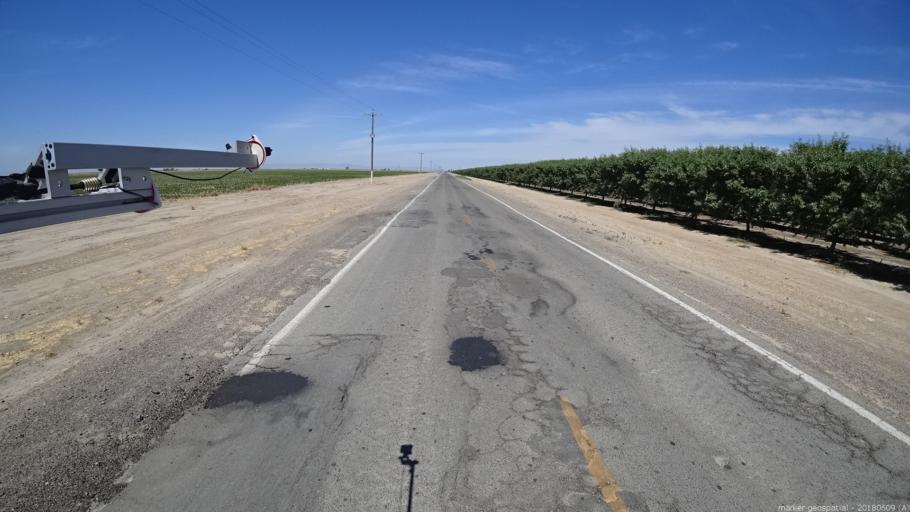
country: US
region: California
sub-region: Fresno County
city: Firebaugh
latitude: 36.9526
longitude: -120.3298
